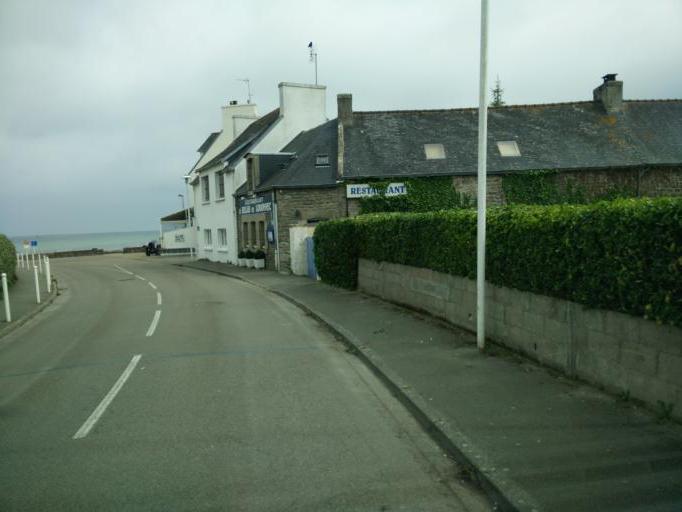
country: FR
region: Brittany
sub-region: Departement du Finistere
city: Loctudy
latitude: 47.8116
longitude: -4.1766
